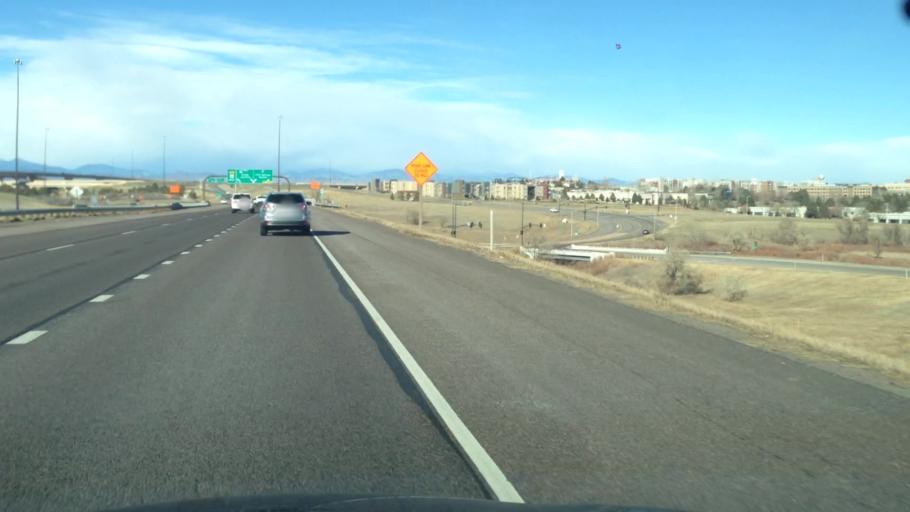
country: US
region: Colorado
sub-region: Douglas County
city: Meridian
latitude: 39.5533
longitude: -104.8595
